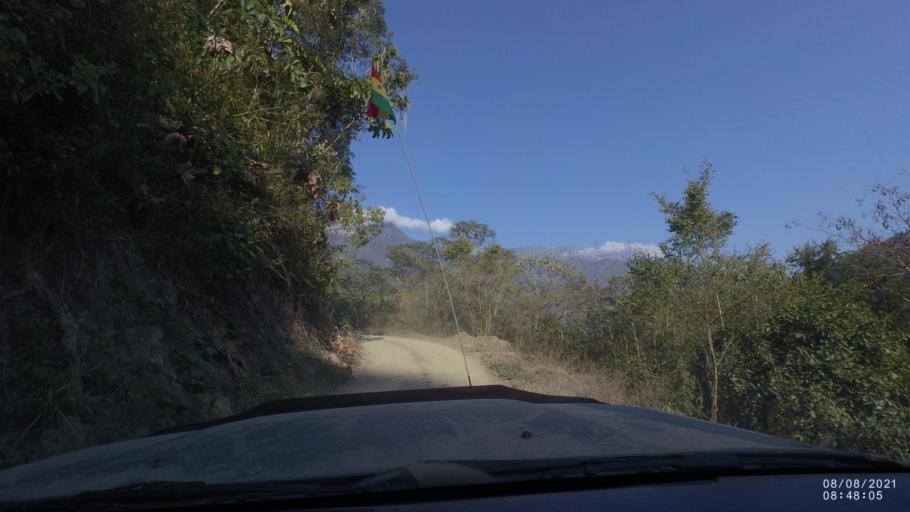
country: BO
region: La Paz
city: Quime
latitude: -16.5301
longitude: -66.7542
